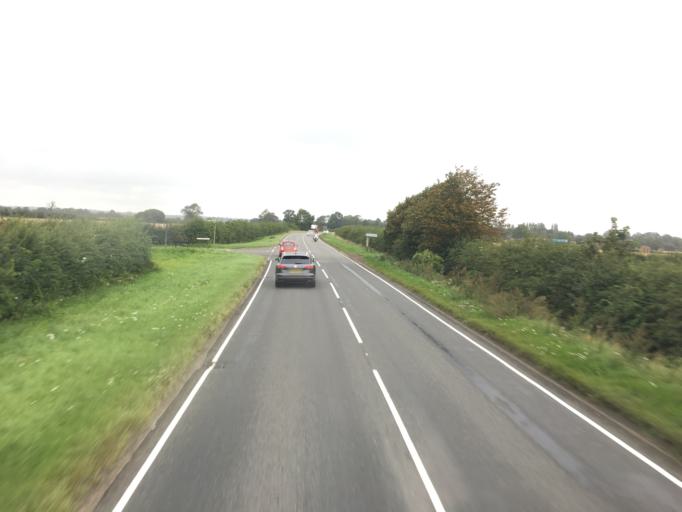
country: GB
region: England
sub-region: Leicestershire
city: Lutterworth
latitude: 52.4170
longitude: -1.2322
